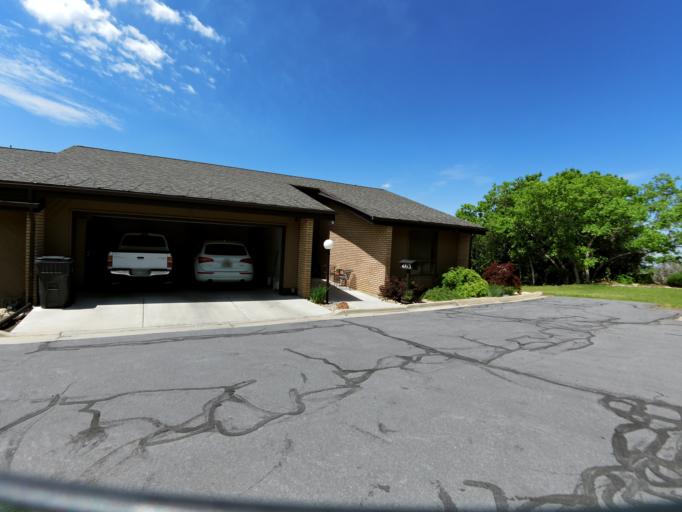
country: US
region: Utah
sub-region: Weber County
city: Uintah
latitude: 41.1757
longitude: -111.9281
